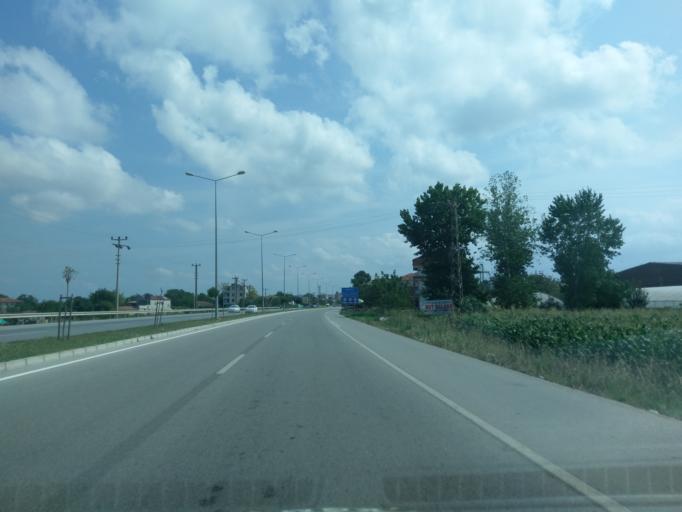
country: TR
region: Samsun
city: Bafra
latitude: 41.5724
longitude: 35.8694
